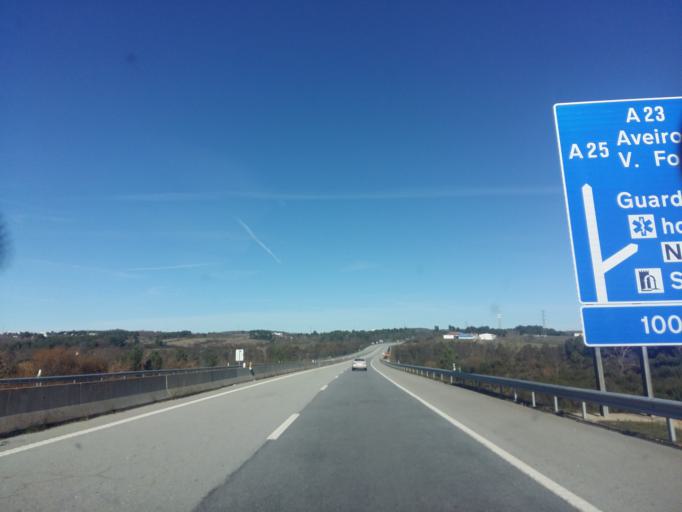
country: PT
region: Guarda
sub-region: Guarda
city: Guarda
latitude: 40.5120
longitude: -7.2341
